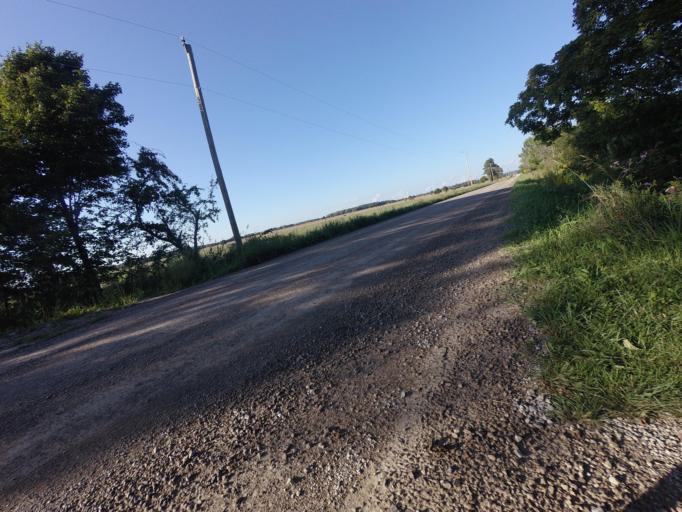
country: CA
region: Ontario
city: Goderich
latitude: 43.7565
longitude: -81.6801
